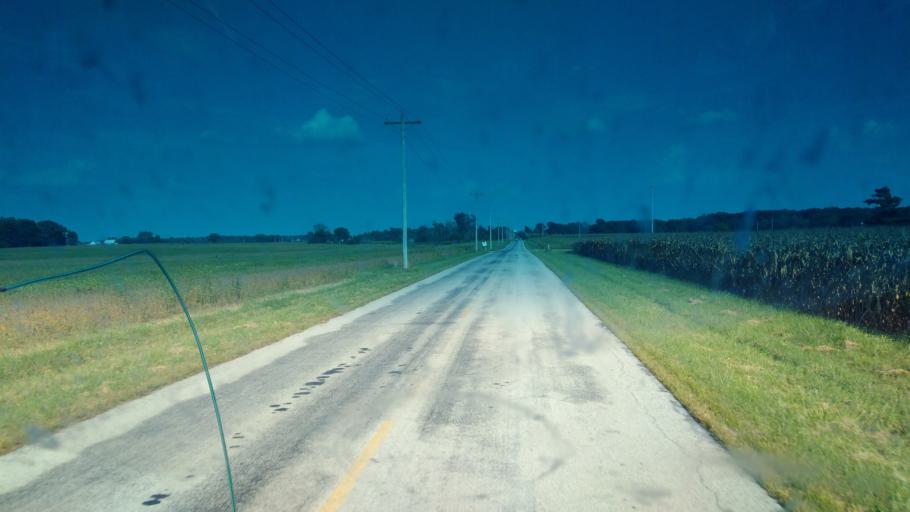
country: US
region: Ohio
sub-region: Wyandot County
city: Carey
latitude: 40.9051
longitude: -83.3950
